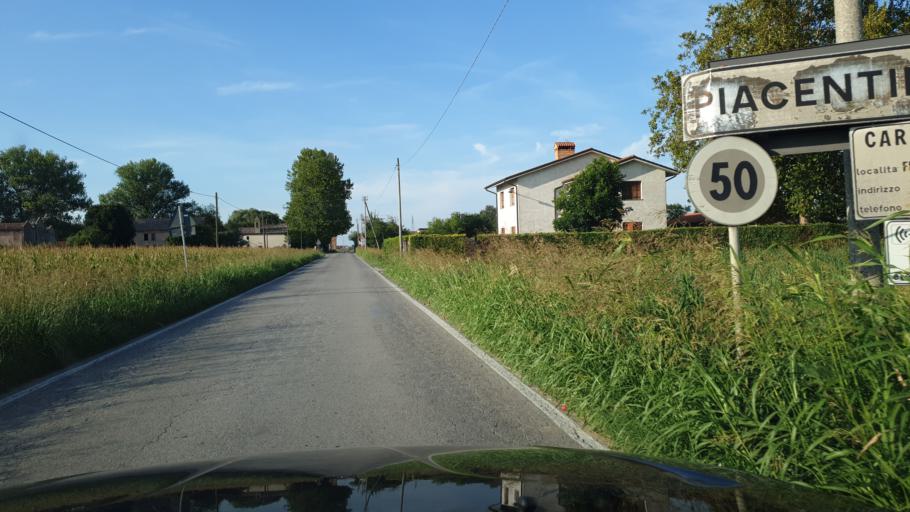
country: IT
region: Veneto
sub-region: Provincia di Rovigo
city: Fiesso Umbertiano
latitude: 44.9420
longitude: 11.6192
